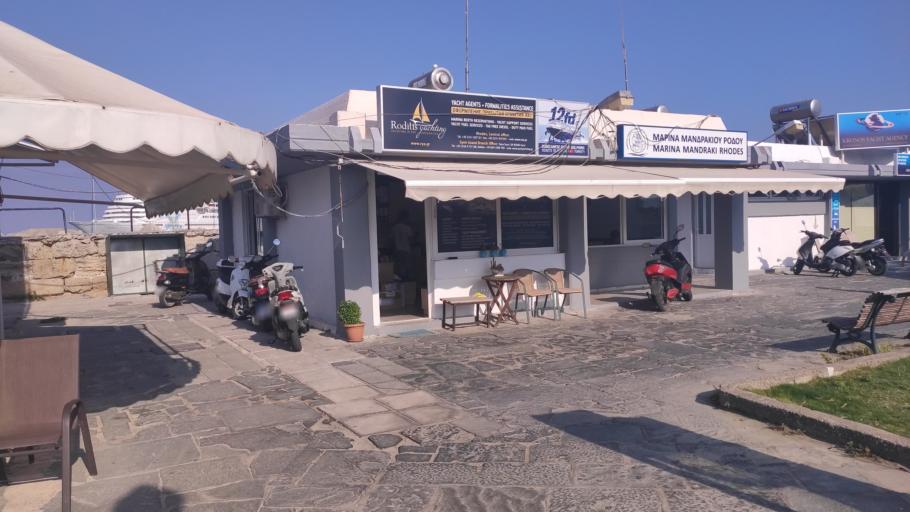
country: GR
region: South Aegean
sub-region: Nomos Dodekanisou
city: Rodos
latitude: 36.4478
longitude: 28.2276
